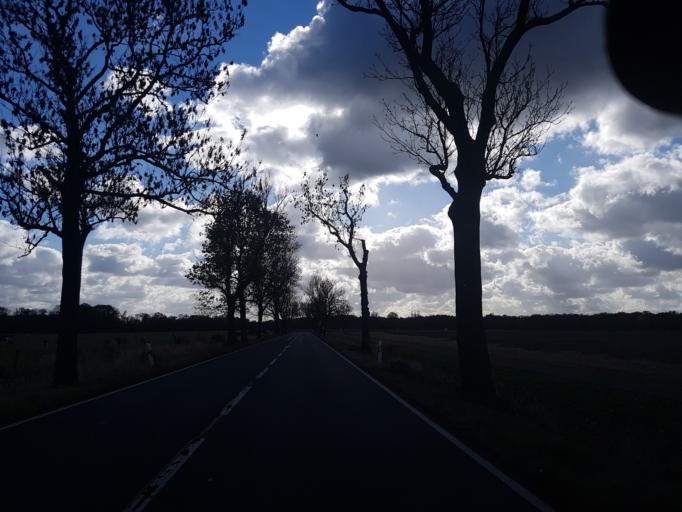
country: DE
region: Brandenburg
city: Nauen
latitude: 52.6508
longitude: 12.9254
